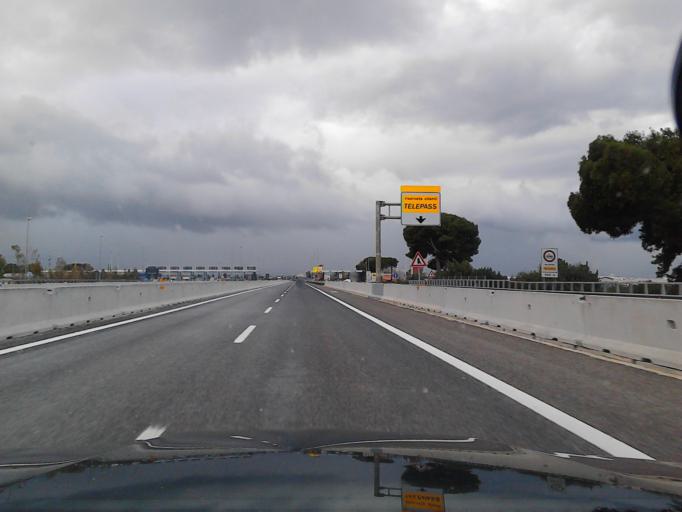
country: IT
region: Apulia
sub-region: Provincia di Bari
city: Modugno
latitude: 41.0917
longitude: 16.7809
